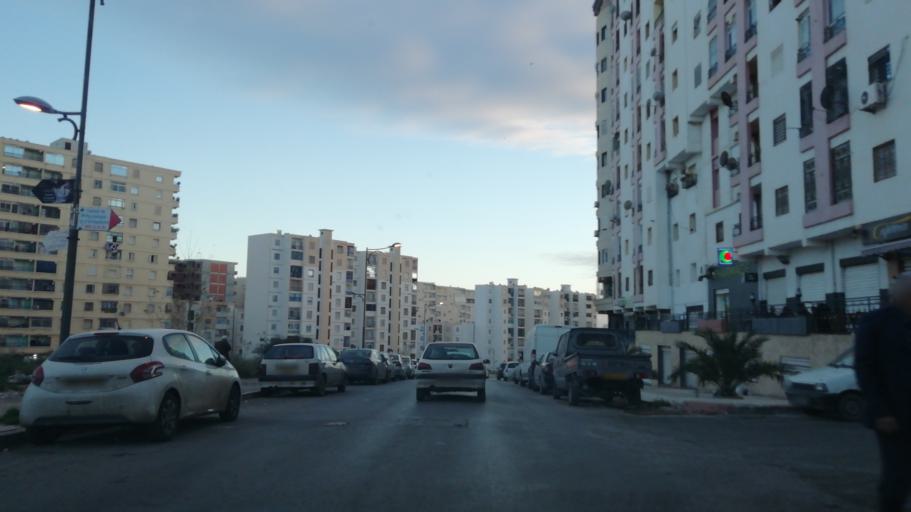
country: DZ
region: Oran
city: Bir el Djir
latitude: 35.7014
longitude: -0.5615
